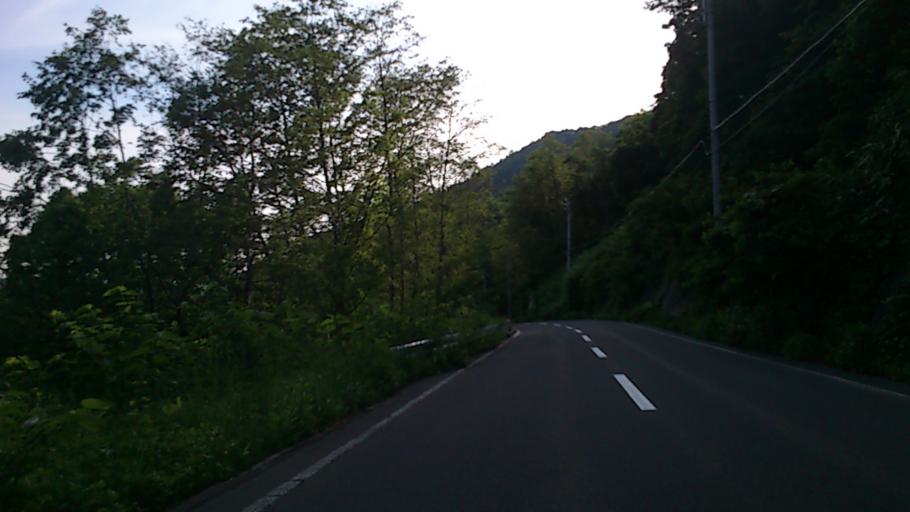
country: JP
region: Aomori
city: Kuroishi
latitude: 40.6489
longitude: 140.7569
